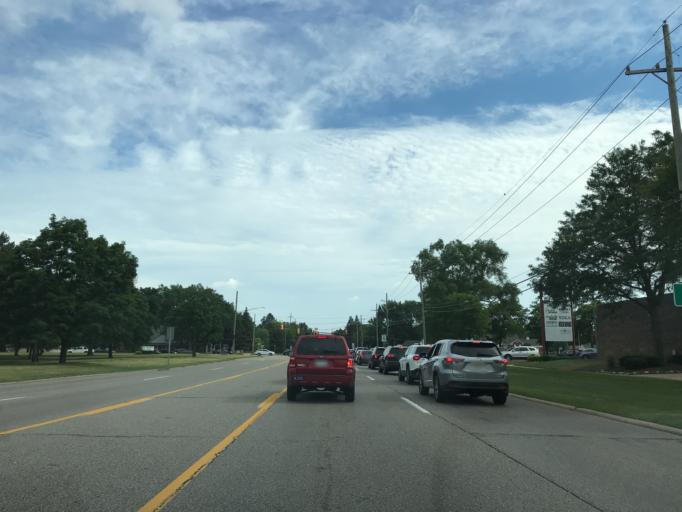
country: US
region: Michigan
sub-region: Oakland County
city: Farmington
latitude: 42.4280
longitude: -83.3555
